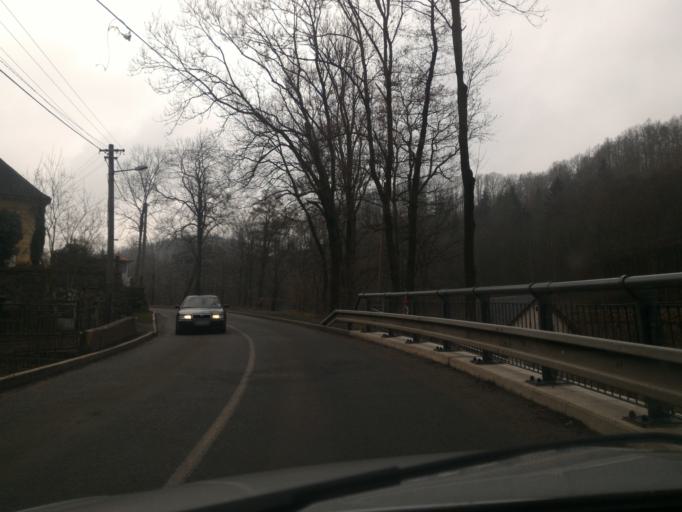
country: CZ
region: Liberecky
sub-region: Okres Liberec
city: Frydlant
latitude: 50.9150
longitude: 15.0812
